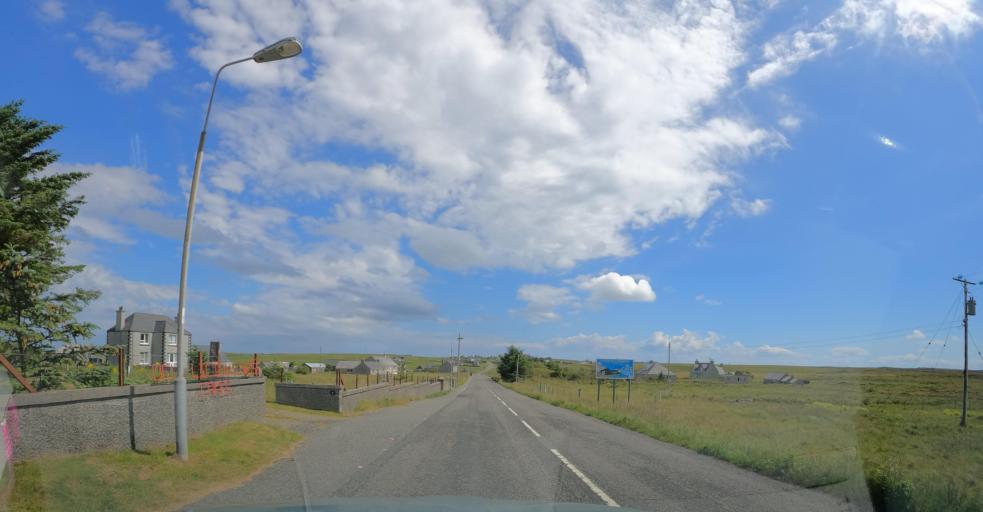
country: GB
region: Scotland
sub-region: Eilean Siar
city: Isle of Lewis
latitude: 58.4685
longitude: -6.2927
